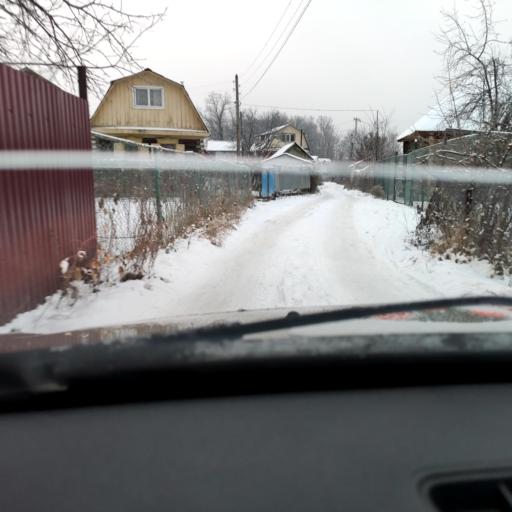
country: RU
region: Bashkortostan
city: Ufa
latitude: 54.6963
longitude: 55.8929
